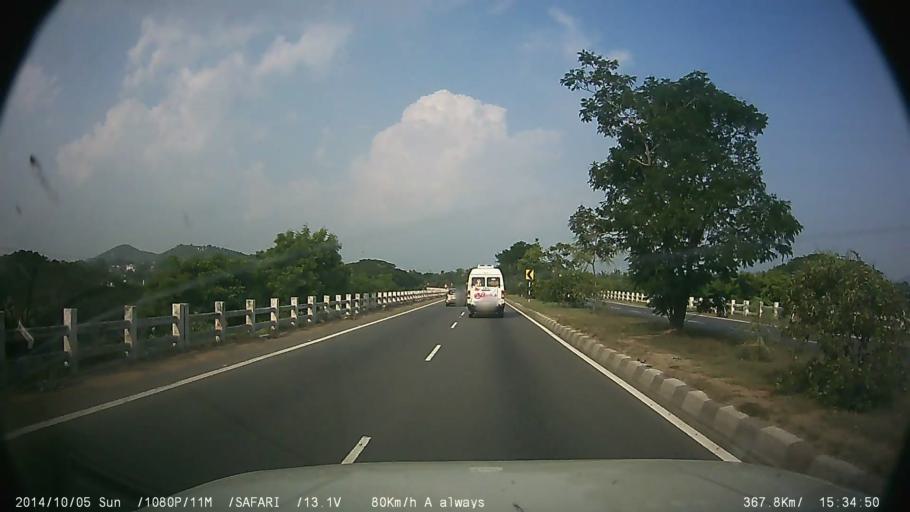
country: IN
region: Tamil Nadu
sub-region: Kancheepuram
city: Chengalpattu
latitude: 12.7050
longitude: 79.9738
